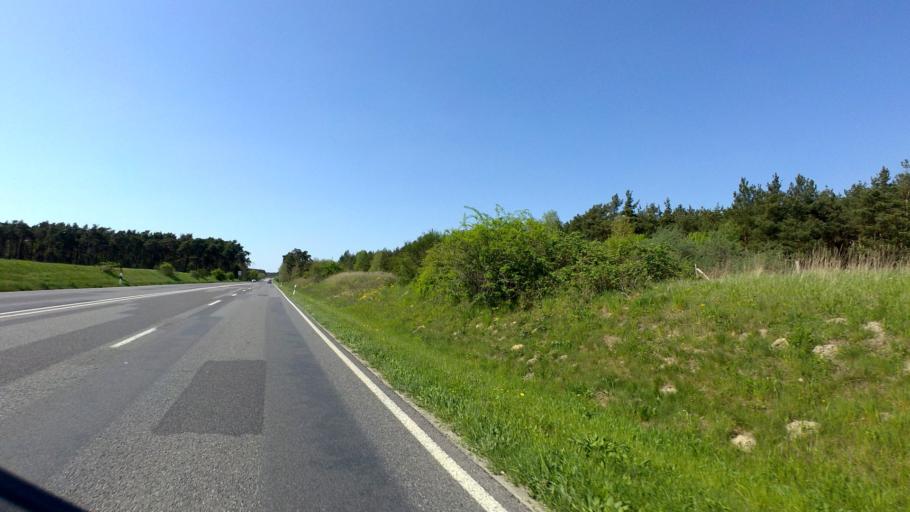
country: DE
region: Brandenburg
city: Beeskow
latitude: 52.1920
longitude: 14.2786
